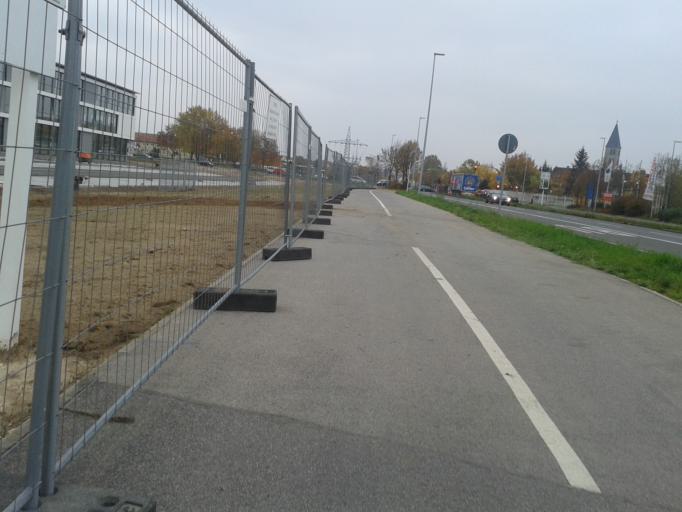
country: DE
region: Bavaria
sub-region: Upper Franconia
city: Bamberg
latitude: 49.9133
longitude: 10.9117
